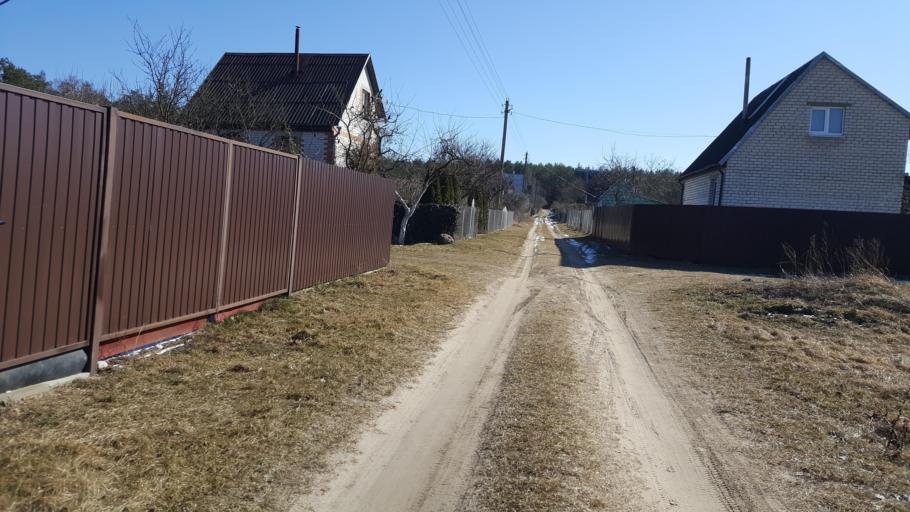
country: BY
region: Brest
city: Kamyanyets
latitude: 52.3685
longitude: 23.8053
